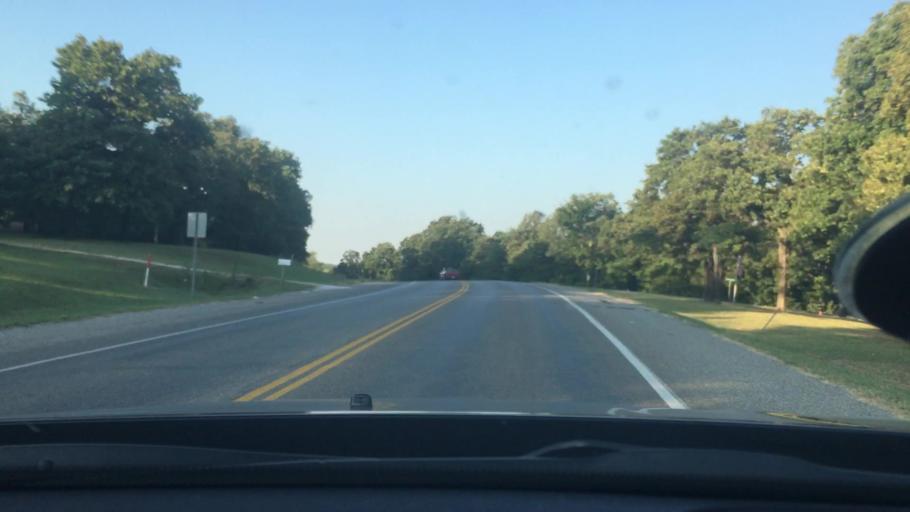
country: US
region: Oklahoma
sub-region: Pontotoc County
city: Byng
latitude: 34.8524
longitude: -96.6778
